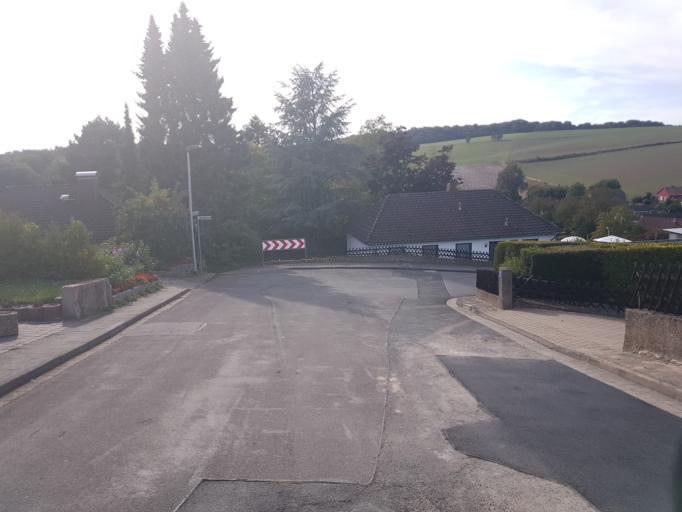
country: DE
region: Lower Saxony
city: Hameln
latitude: 52.1380
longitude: 9.3798
